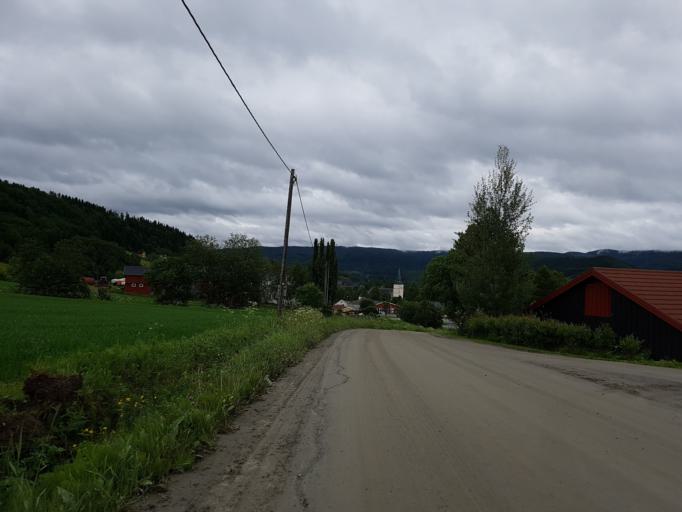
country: NO
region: Sor-Trondelag
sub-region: Selbu
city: Mebonden
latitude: 63.2216
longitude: 11.0406
